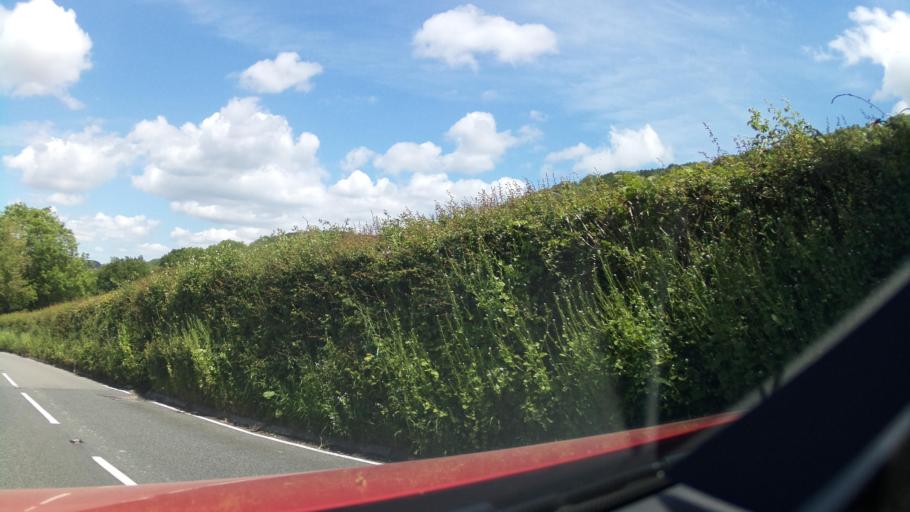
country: GB
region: Wales
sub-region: Monmouthshire
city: Mitchel Troy
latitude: 51.7865
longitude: -2.7172
